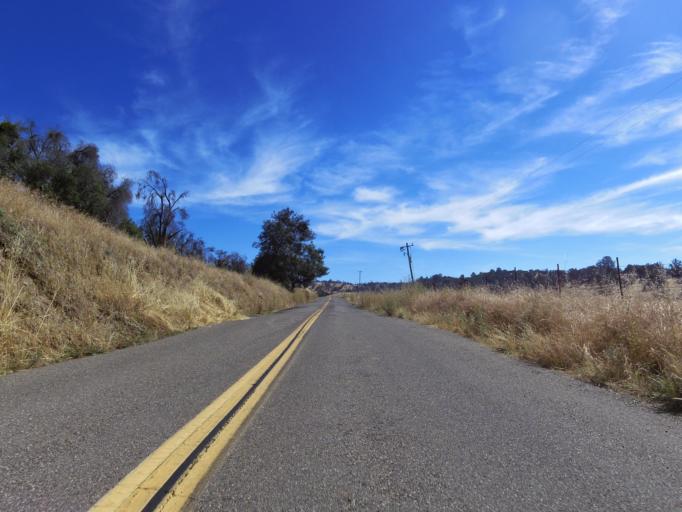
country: US
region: California
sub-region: Mariposa County
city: Mariposa
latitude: 37.3725
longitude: -119.9675
